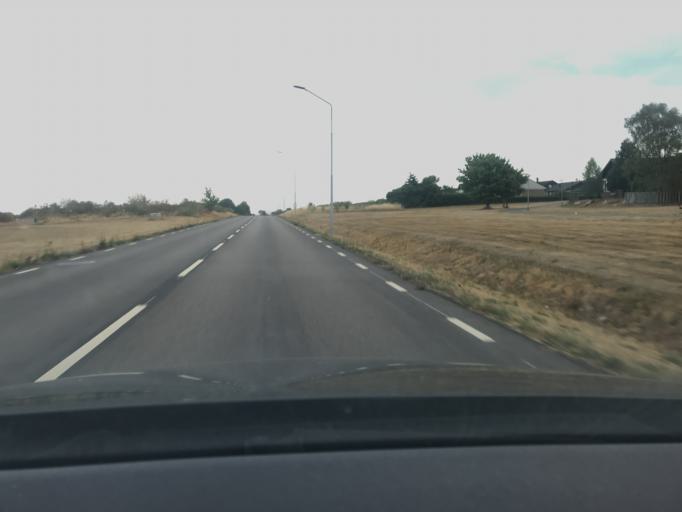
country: SE
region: Skane
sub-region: Simrishamns Kommun
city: Simrishamn
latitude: 55.5443
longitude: 14.3528
